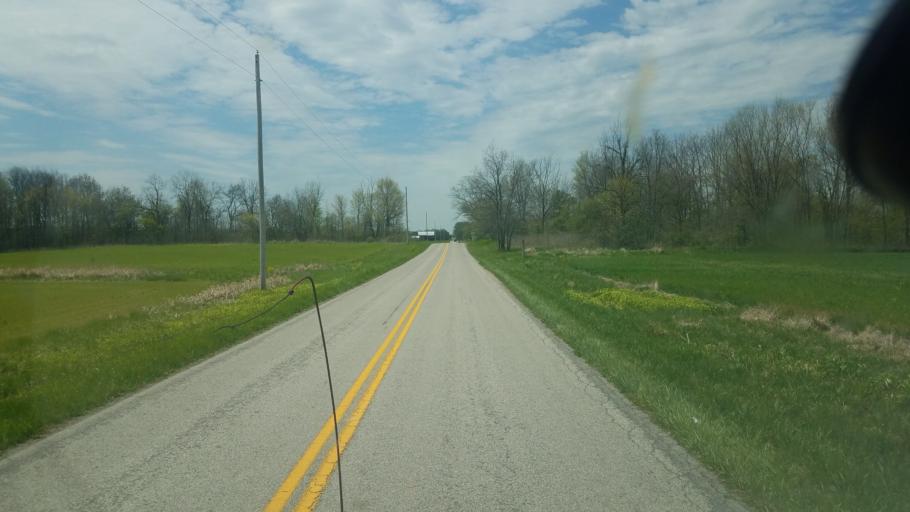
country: US
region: Ohio
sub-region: Hardin County
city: Ada
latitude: 40.7935
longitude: -83.9136
